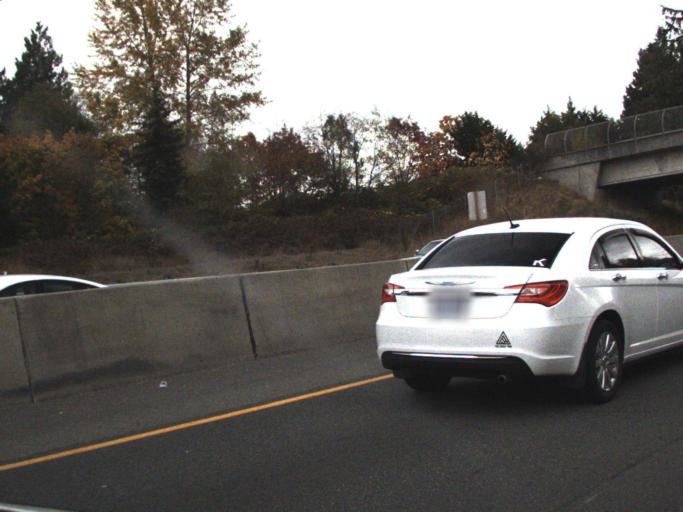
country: US
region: Washington
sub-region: Snohomish County
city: Martha Lake
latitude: 47.8647
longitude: -122.2749
